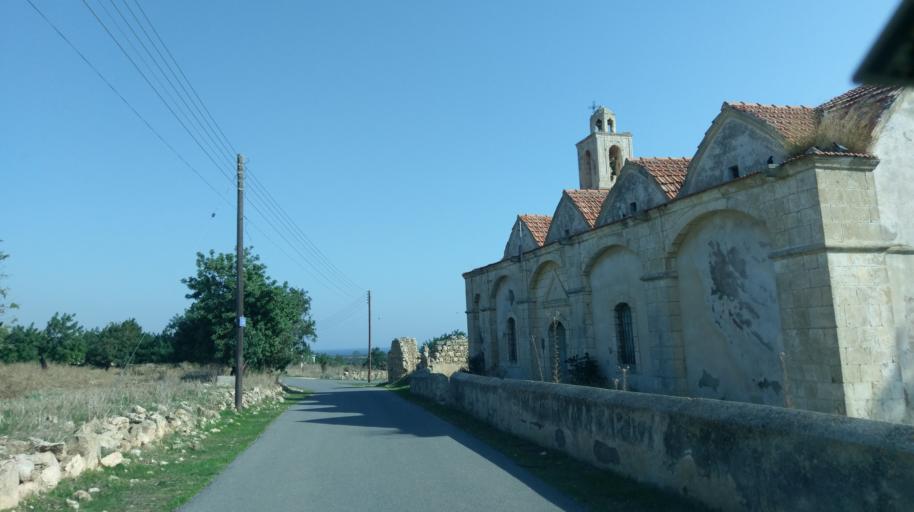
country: CY
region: Ammochostos
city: Leonarisso
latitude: 35.4297
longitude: 34.1349
